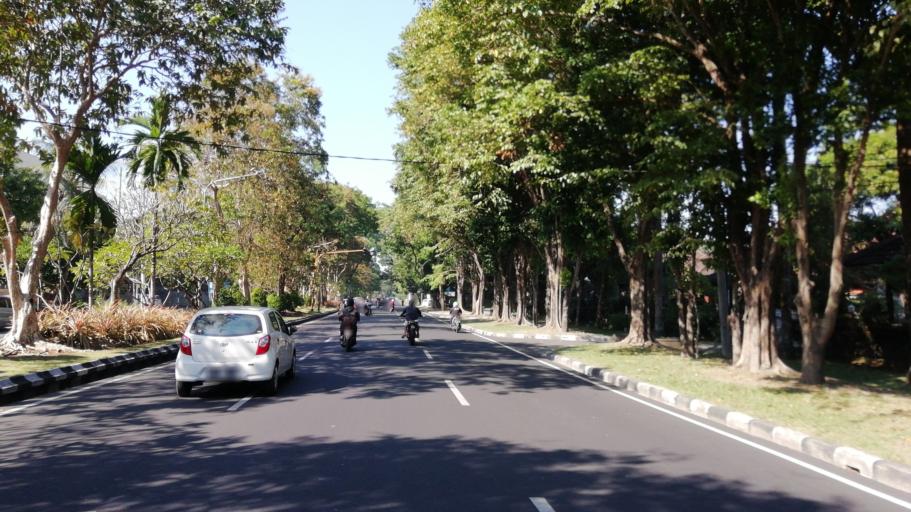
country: ID
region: Bali
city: Banjar Batanpoh
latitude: -8.6694
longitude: 115.2385
